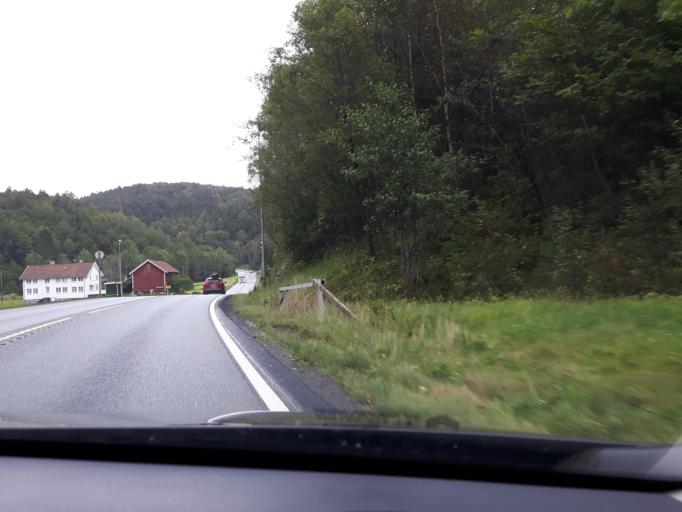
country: NO
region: Vest-Agder
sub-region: Marnardal
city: Helland
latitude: 58.0770
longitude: 7.6057
